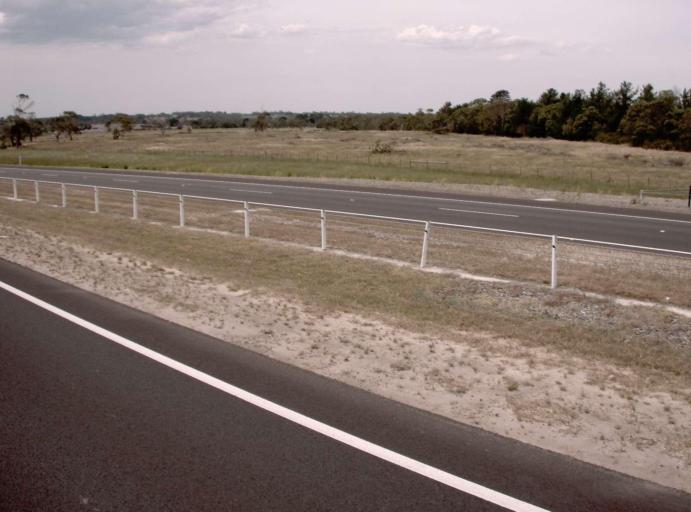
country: AU
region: Victoria
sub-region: Mornington Peninsula
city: Moorooduc
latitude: -38.2072
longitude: 145.1323
